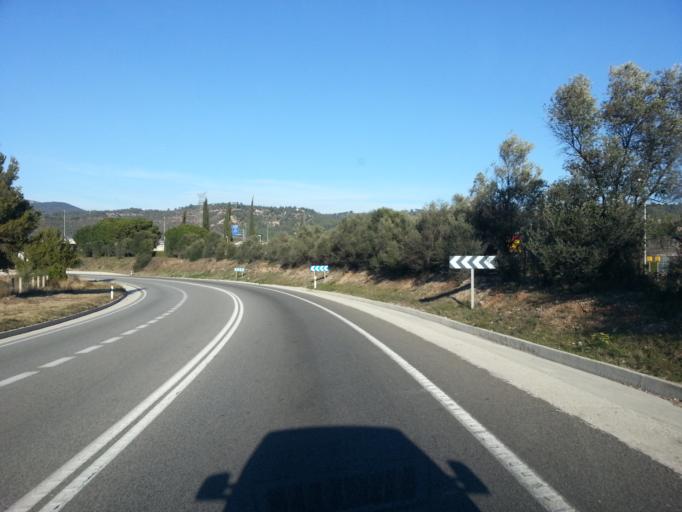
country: ES
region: Catalonia
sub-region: Provincia de Barcelona
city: Abrera
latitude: 41.5257
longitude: 1.9057
